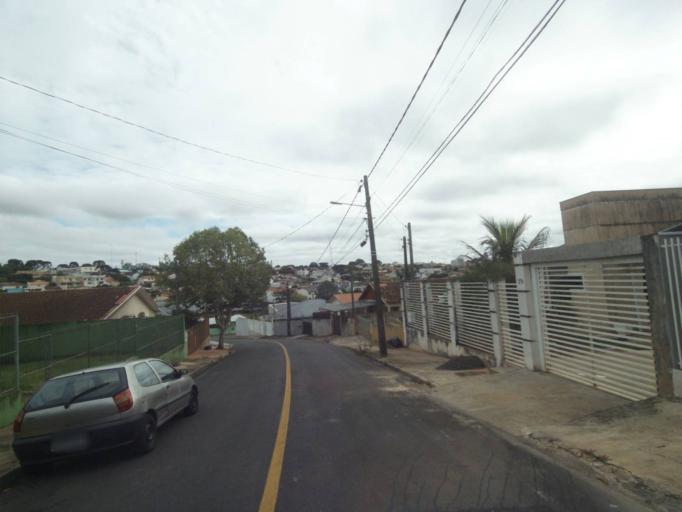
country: BR
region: Parana
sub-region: Telemaco Borba
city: Telemaco Borba
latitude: -24.3358
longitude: -50.6217
